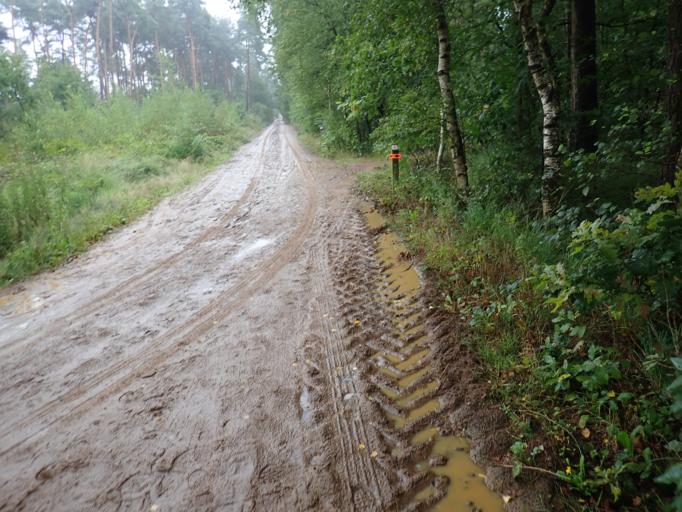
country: BE
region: Flanders
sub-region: Provincie Antwerpen
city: Lille
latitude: 51.2781
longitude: 4.8130
